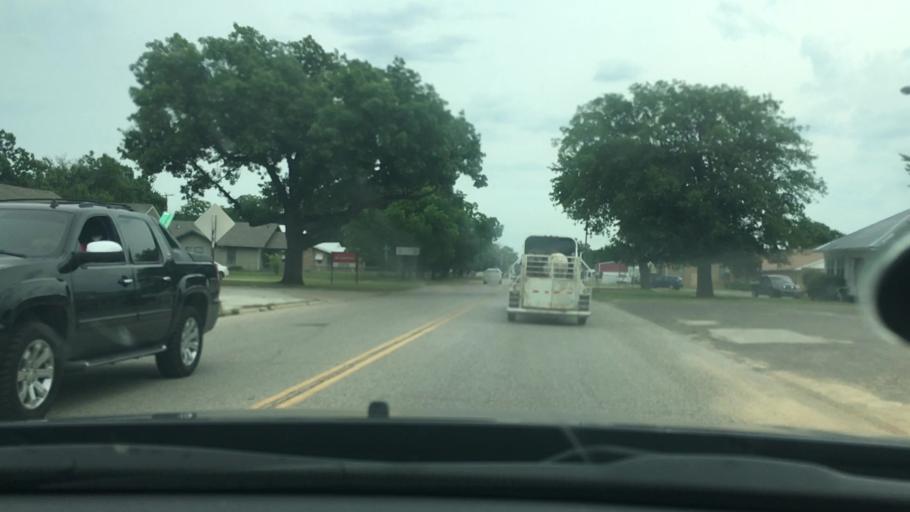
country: US
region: Oklahoma
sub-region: Love County
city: Marietta
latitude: 33.9377
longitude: -97.1249
